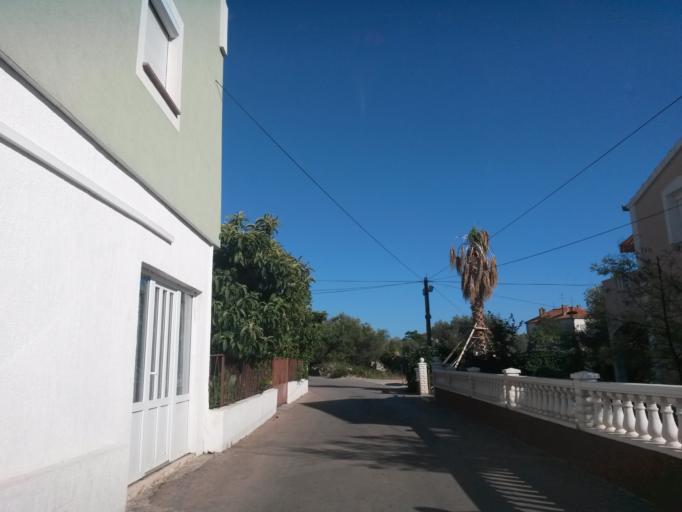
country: HR
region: Sibensko-Kniniska
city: Rogoznica
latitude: 43.5348
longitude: 15.9651
